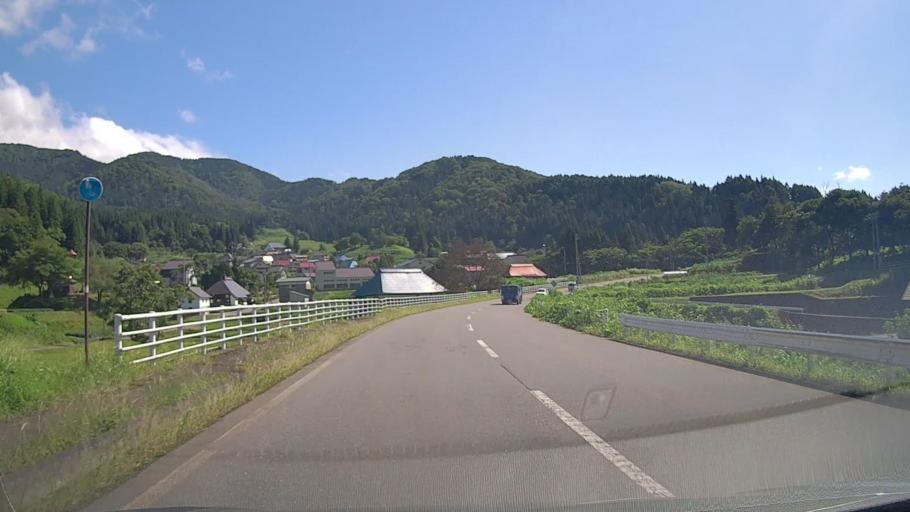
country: JP
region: Nagano
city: Iiyama
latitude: 36.9585
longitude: 138.4483
